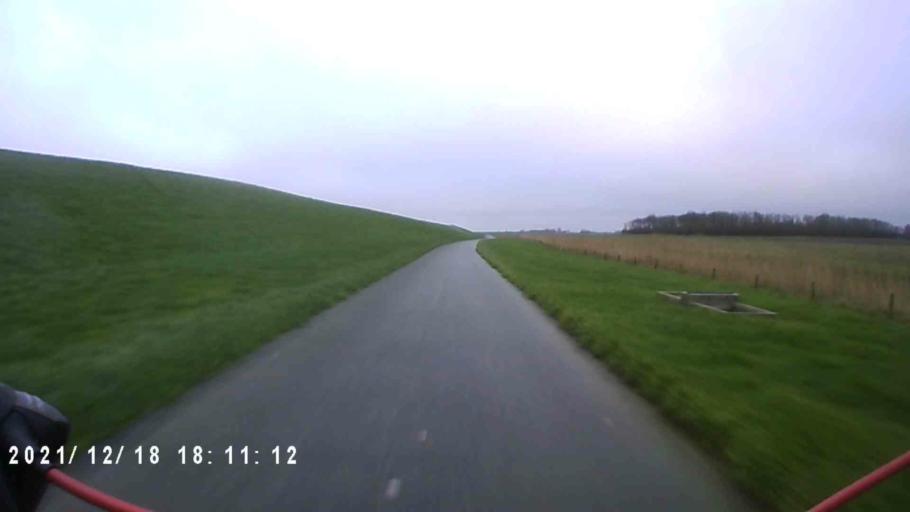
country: NL
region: Friesland
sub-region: Gemeente Dongeradeel
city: Ternaard
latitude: 53.3894
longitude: 5.9421
